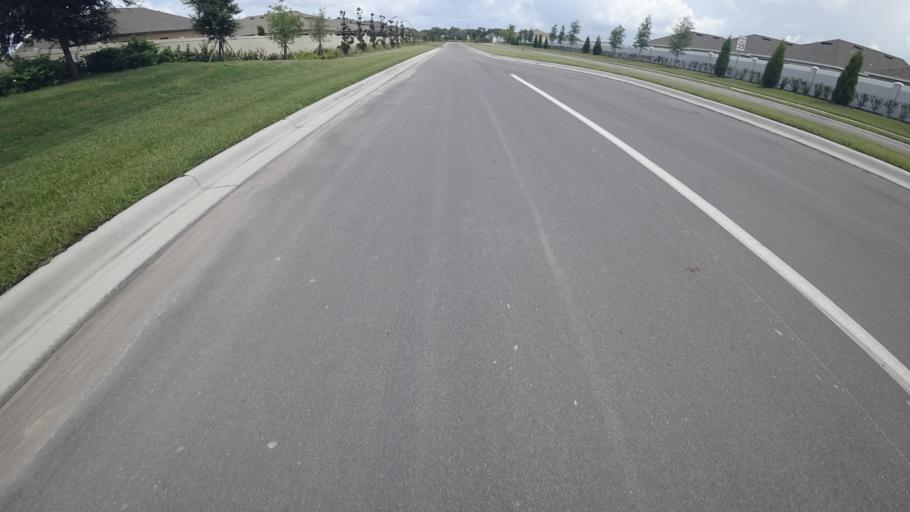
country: US
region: Florida
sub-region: Manatee County
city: Ellenton
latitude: 27.5473
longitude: -82.5159
